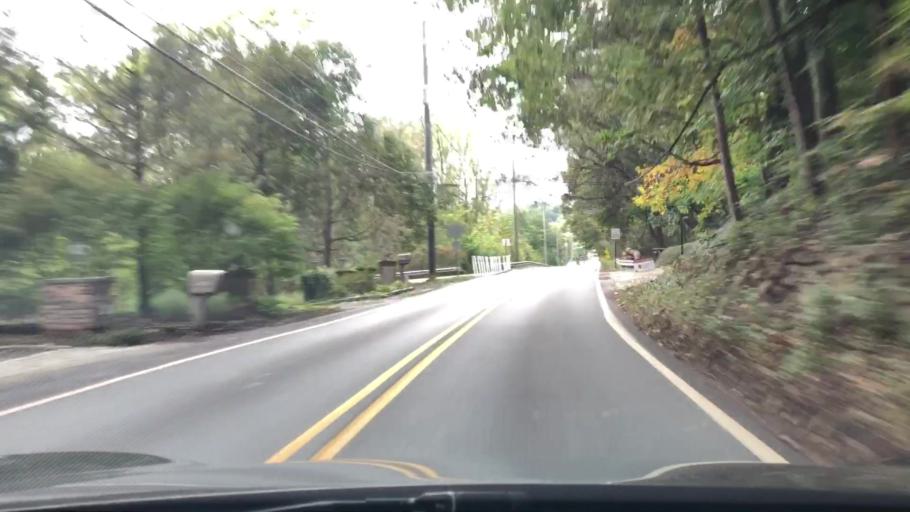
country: US
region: Pennsylvania
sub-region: Delaware County
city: Radnor
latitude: 40.0363
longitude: -75.3665
